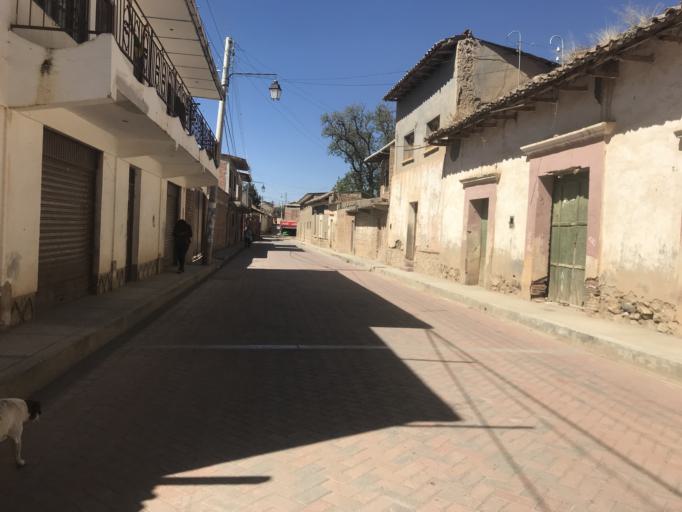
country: BO
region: Cochabamba
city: Tarata
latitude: -17.6143
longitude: -66.0264
